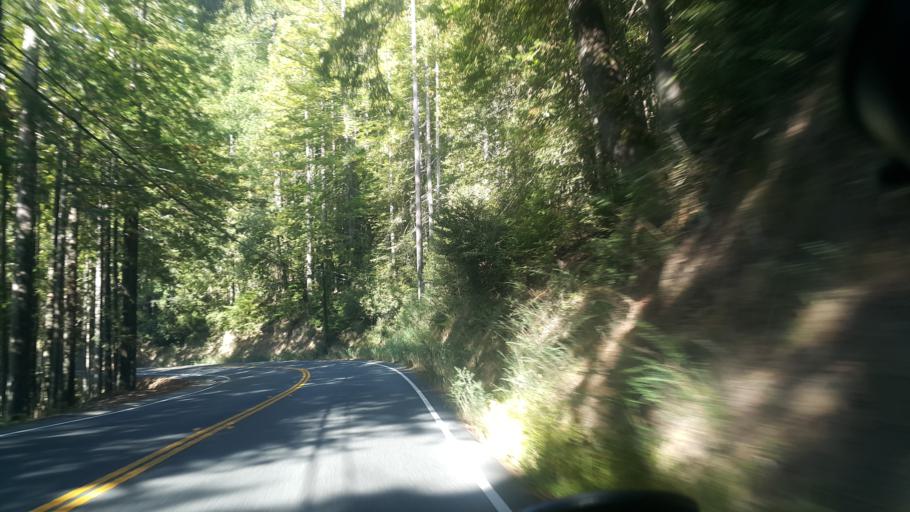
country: US
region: California
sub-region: Mendocino County
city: Fort Bragg
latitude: 39.4071
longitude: -123.7294
